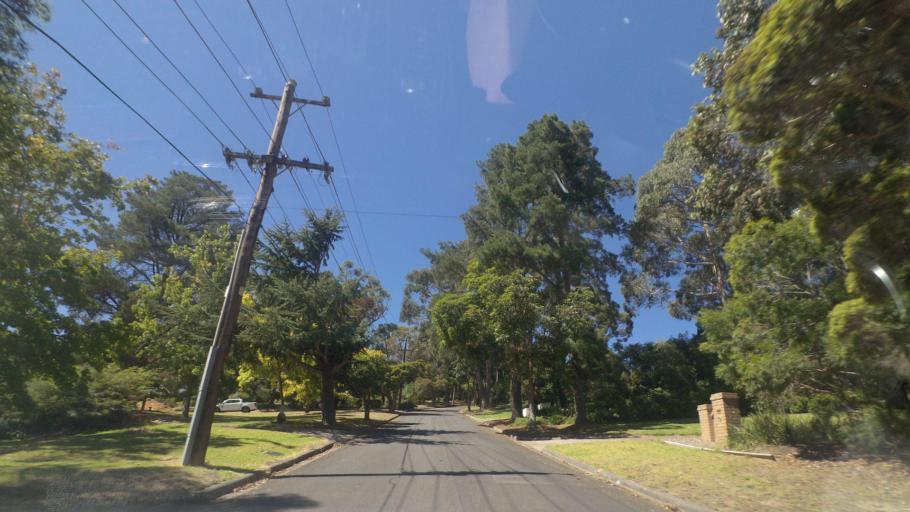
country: AU
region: Victoria
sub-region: Manningham
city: Donvale
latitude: -37.7906
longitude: 145.1865
